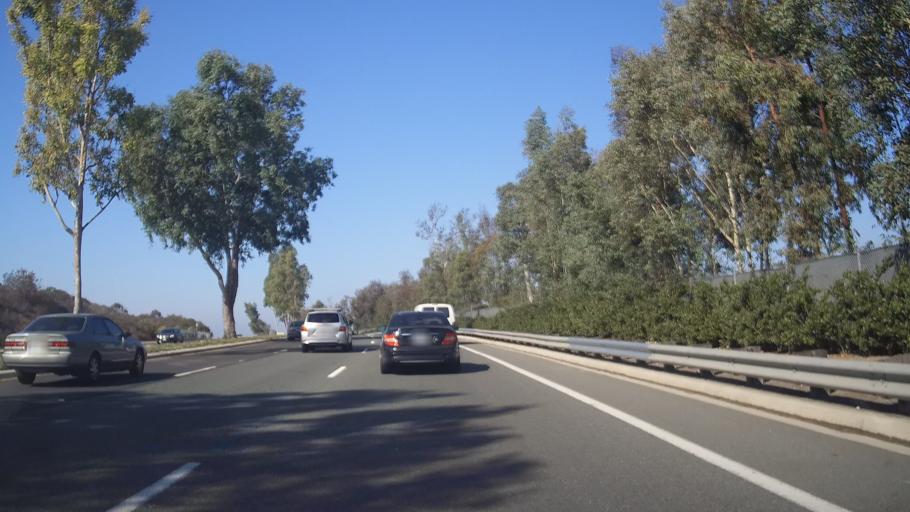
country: US
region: California
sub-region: San Diego County
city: Poway
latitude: 33.0102
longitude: -117.0969
